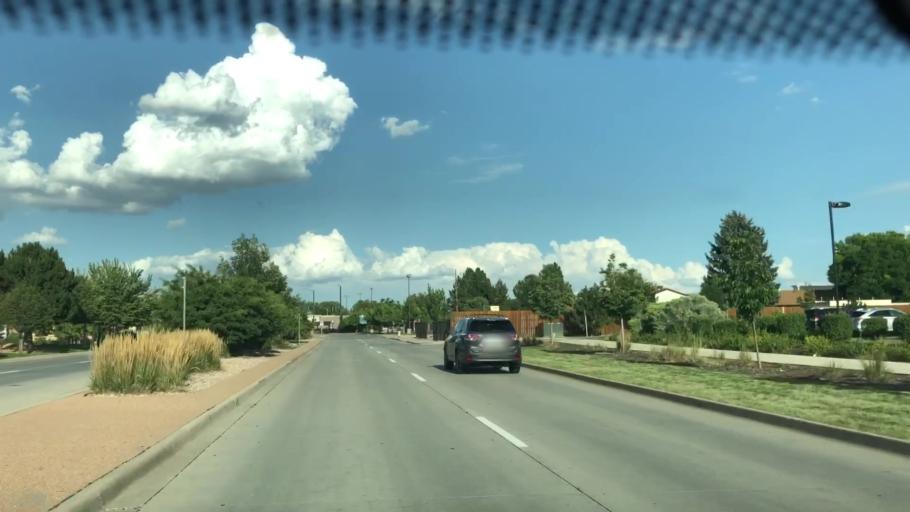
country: US
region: Colorado
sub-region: Douglas County
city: Parker
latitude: 39.5184
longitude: -104.7700
